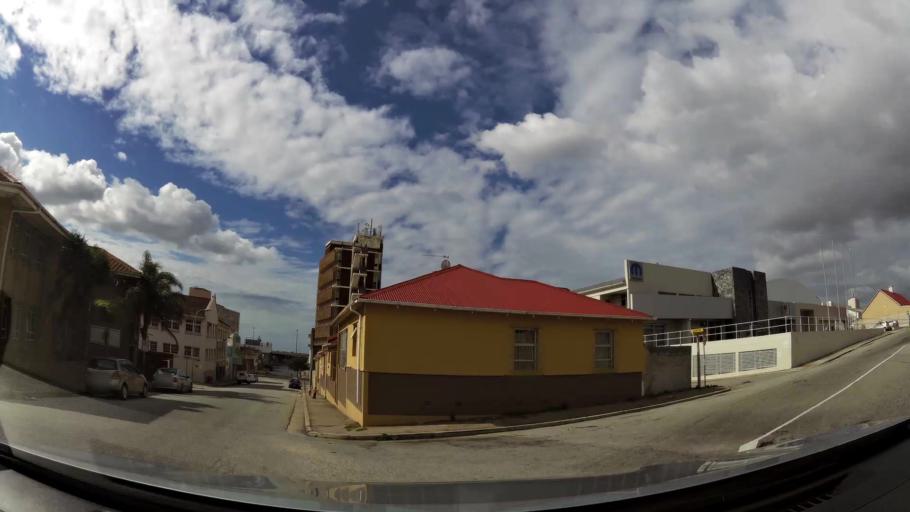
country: ZA
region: Eastern Cape
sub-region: Nelson Mandela Bay Metropolitan Municipality
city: Port Elizabeth
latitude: -33.9484
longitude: 25.6054
